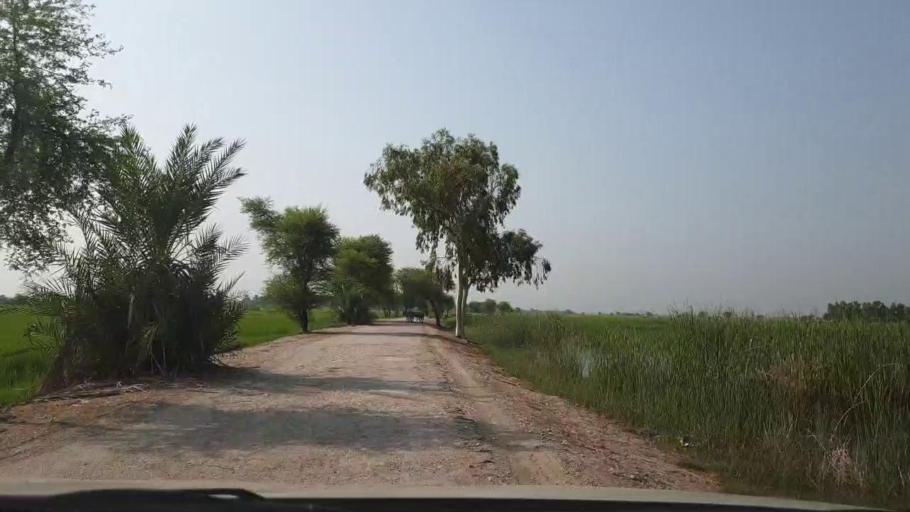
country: PK
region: Sindh
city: Goth Garelo
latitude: 27.4694
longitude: 68.0888
